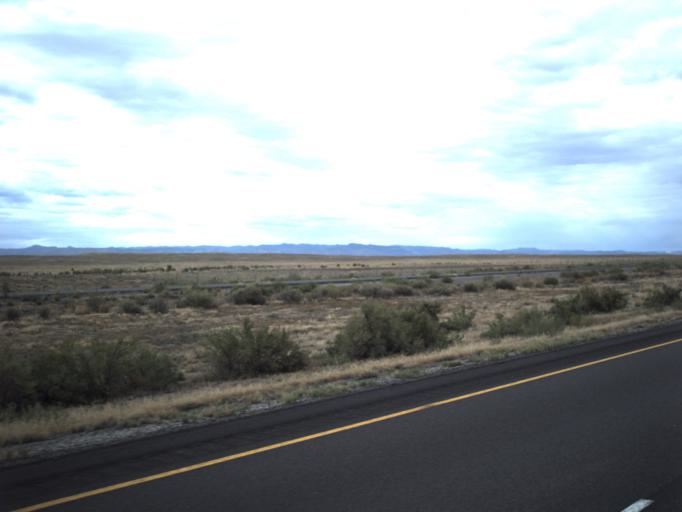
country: US
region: Colorado
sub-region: Mesa County
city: Loma
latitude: 39.0859
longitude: -109.2193
